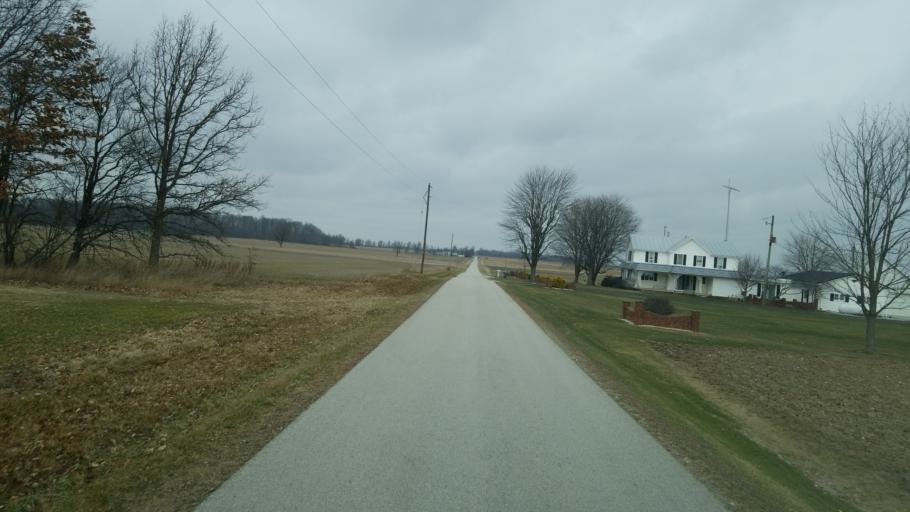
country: US
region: Ohio
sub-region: Hardin County
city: Forest
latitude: 40.7703
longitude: -83.4777
